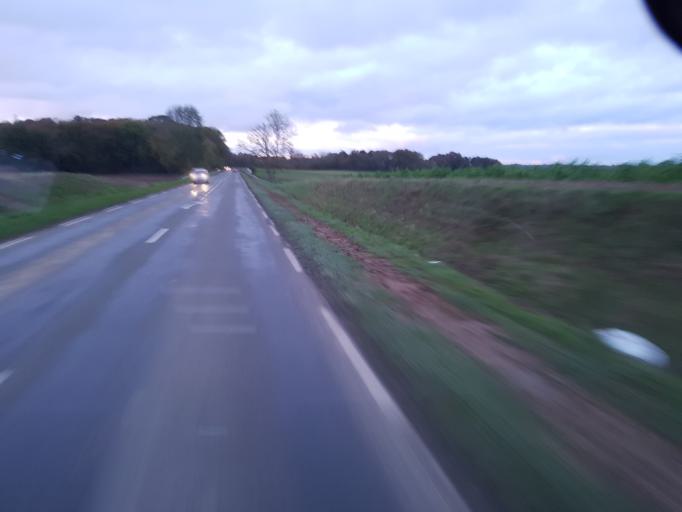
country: FR
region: Picardie
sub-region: Departement de l'Aisne
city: Coincy
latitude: 49.1693
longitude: 3.3754
